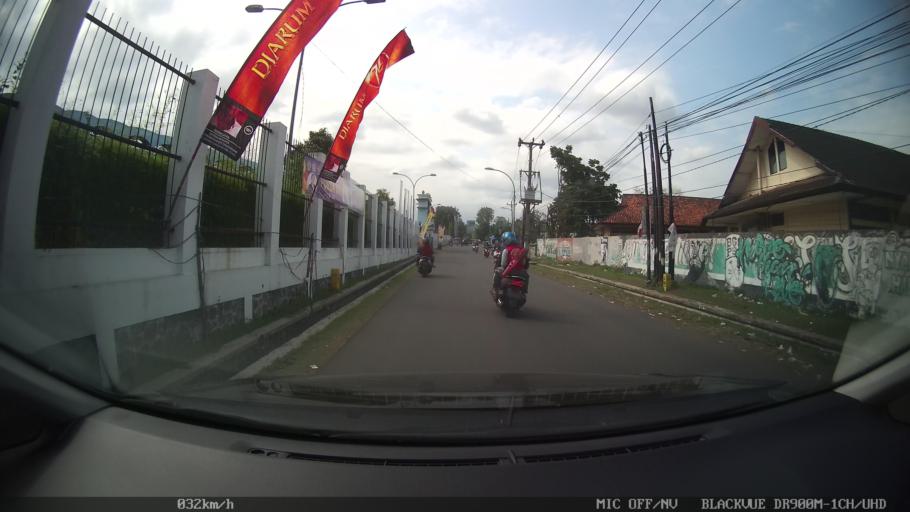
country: ID
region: Daerah Istimewa Yogyakarta
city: Depok
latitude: -7.7514
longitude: 110.4196
